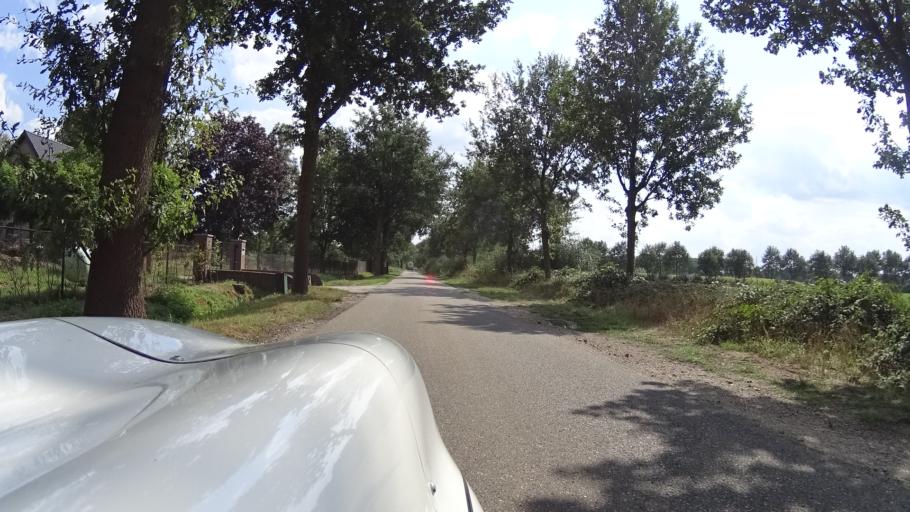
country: NL
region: North Brabant
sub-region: Gemeente Bernheze
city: Loosbroek
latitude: 51.6578
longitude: 5.5138
